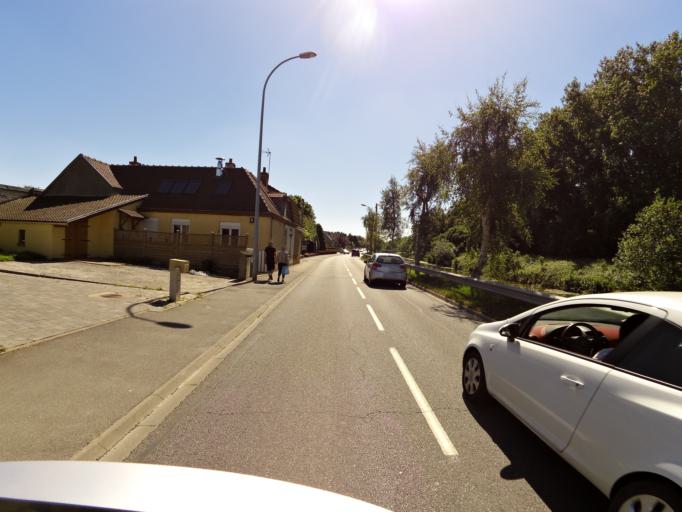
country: FR
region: Nord-Pas-de-Calais
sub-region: Departement du Nord
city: Hoymille
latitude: 50.9745
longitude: 2.4406
